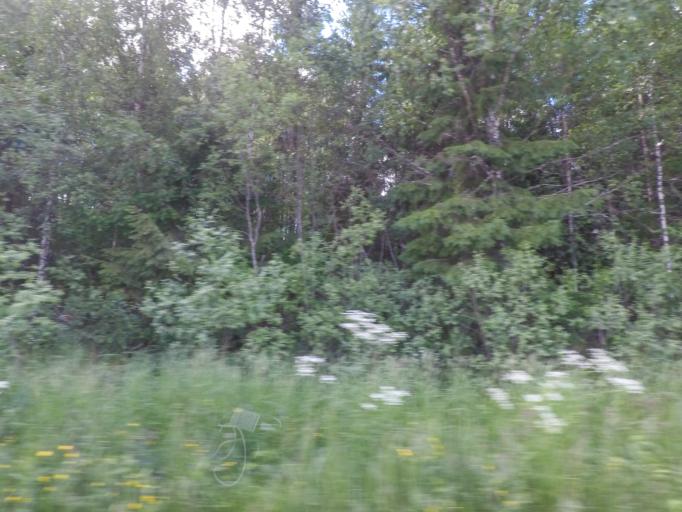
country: FI
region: Central Finland
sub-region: Jyvaeskylae
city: Hankasalmi
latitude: 62.4157
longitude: 26.6408
